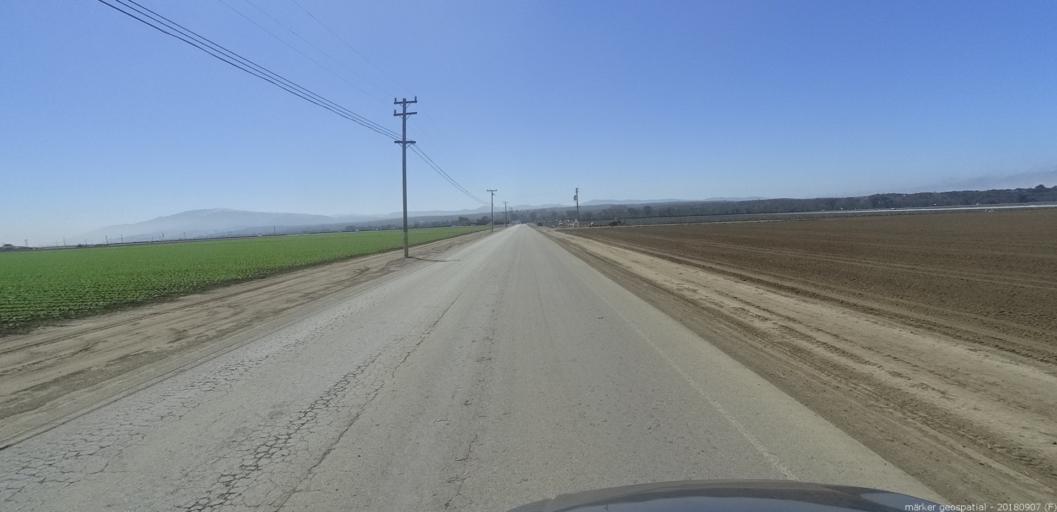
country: US
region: California
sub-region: Monterey County
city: Boronda
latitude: 36.6840
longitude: -121.7350
